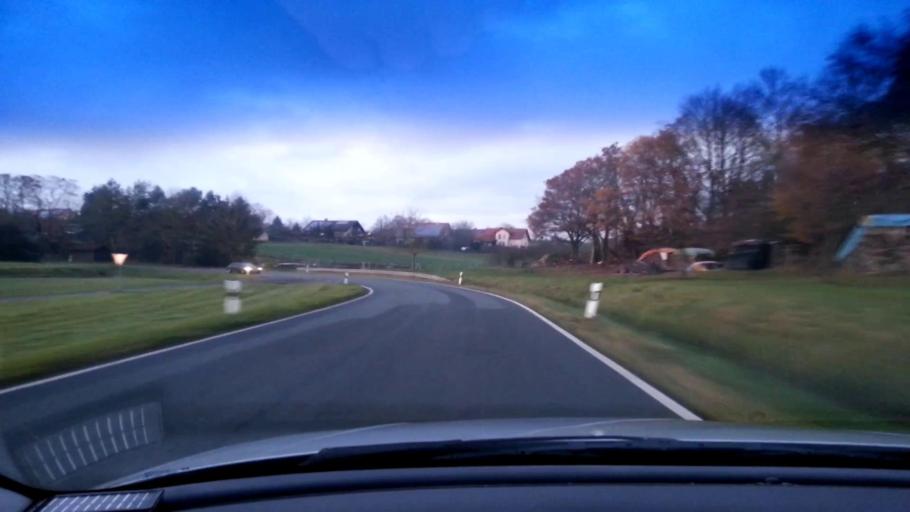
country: DE
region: Bavaria
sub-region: Upper Franconia
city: Frensdorf
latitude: 49.8322
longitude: 10.8761
